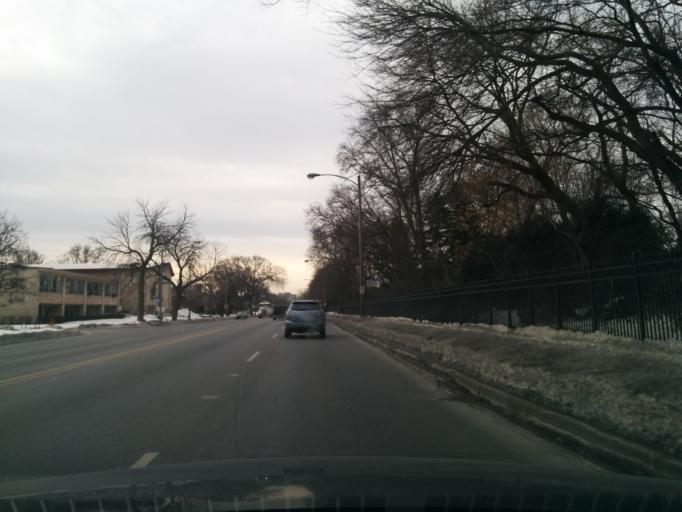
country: US
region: Illinois
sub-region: Cook County
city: River Forest
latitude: 41.9038
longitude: -87.8056
